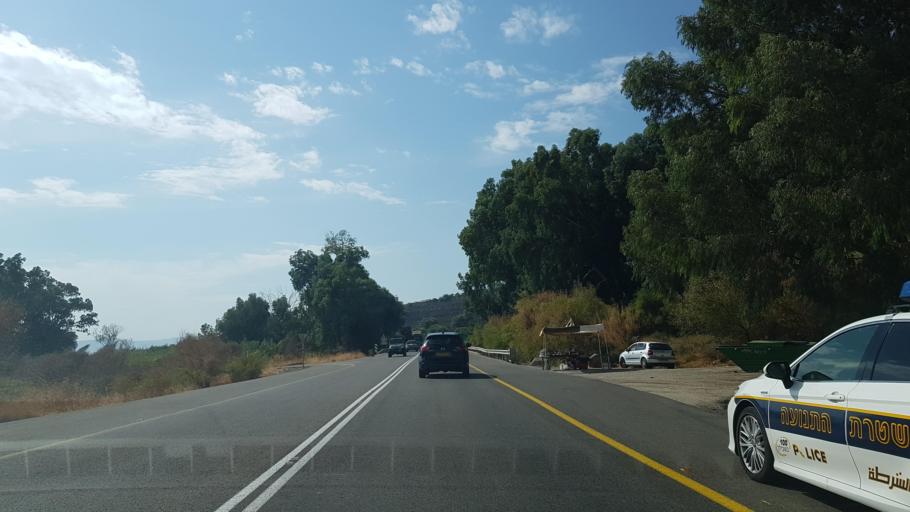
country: SY
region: Quneitra
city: Al Butayhah
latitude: 32.9020
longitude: 35.6160
